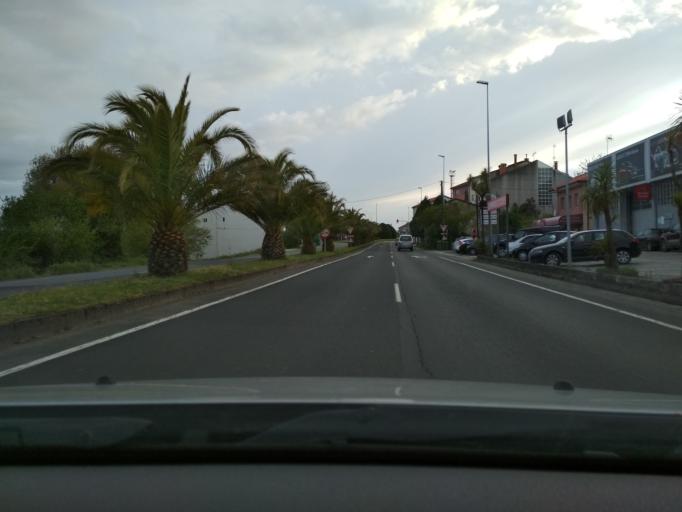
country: ES
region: Galicia
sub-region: Provincia da Coruna
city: Santiago de Compostela
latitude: 42.9005
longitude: -8.5242
